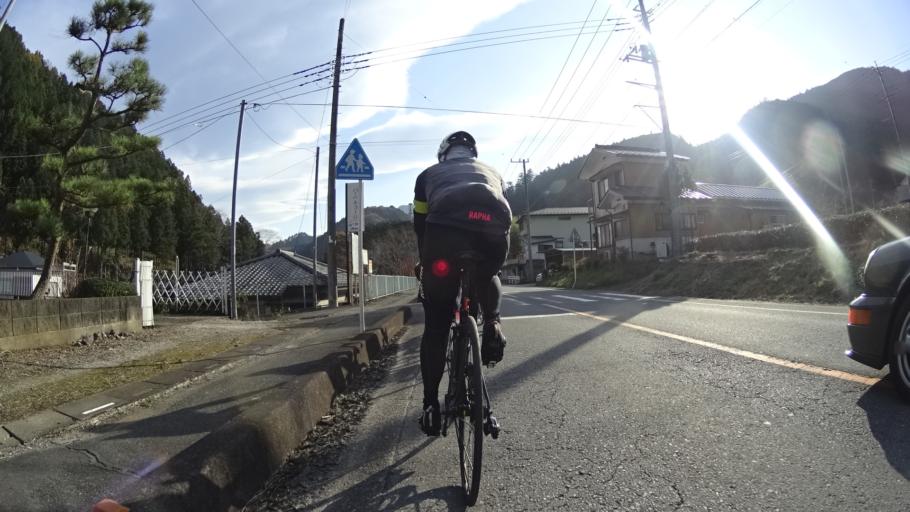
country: JP
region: Tokyo
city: Ome
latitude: 35.8646
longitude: 139.1869
